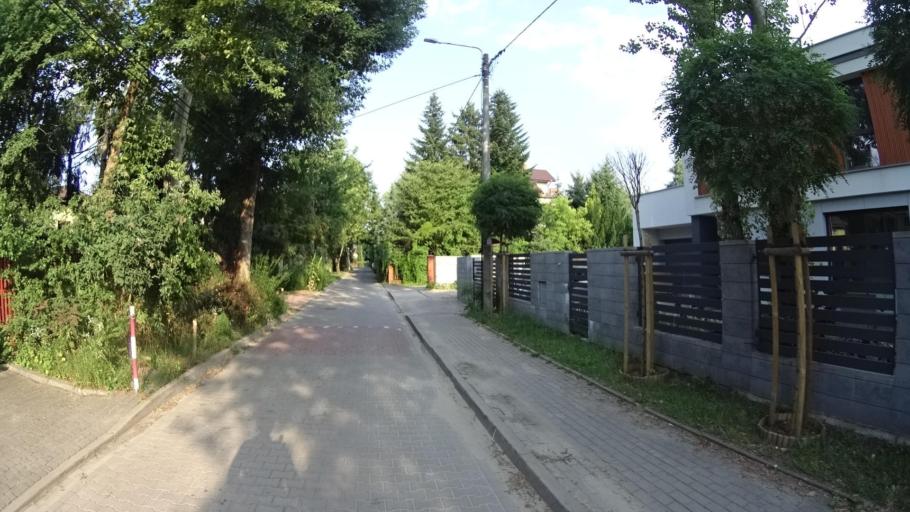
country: PL
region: Masovian Voivodeship
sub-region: Powiat pruszkowski
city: Michalowice
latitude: 52.1772
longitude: 20.8772
